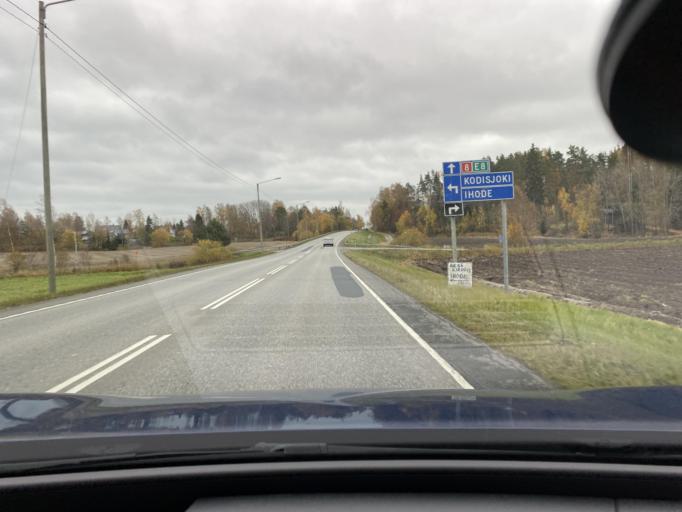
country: FI
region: Varsinais-Suomi
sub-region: Vakka-Suomi
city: Pyhaeranta
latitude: 60.9887
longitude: 21.5843
